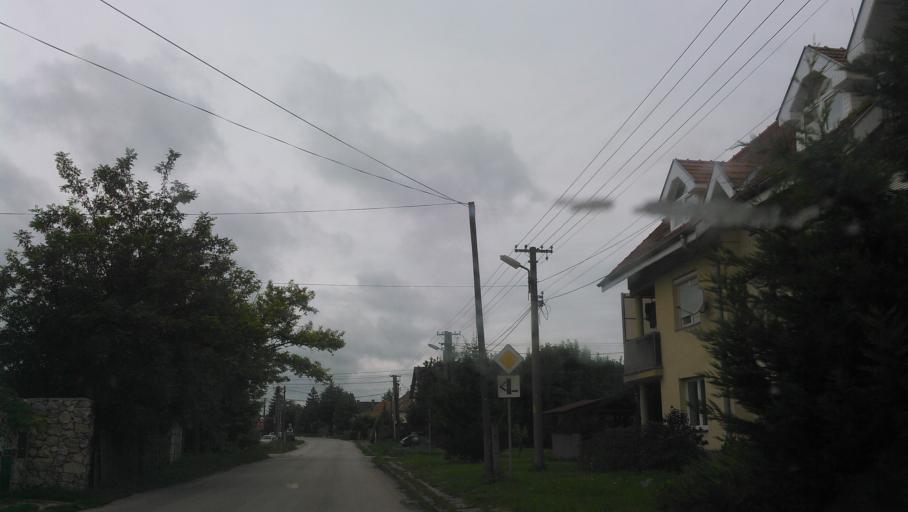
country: SK
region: Trnavsky
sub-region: Okres Dunajska Streda
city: Velky Meder
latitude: 47.8838
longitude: 17.8126
